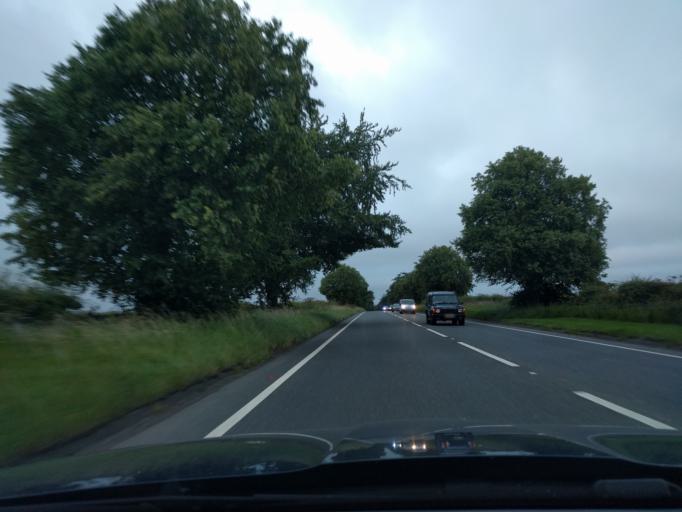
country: GB
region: England
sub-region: Northumberland
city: Hebron
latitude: 55.2056
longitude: -1.7112
